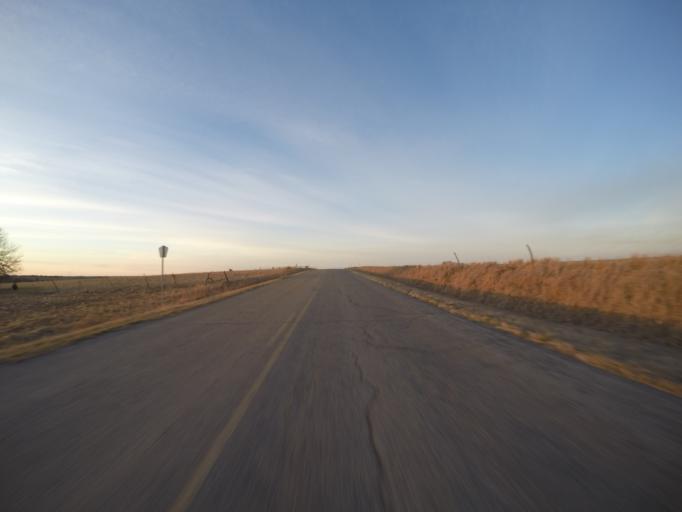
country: US
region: Kansas
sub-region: Clay County
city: Clay Center
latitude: 39.4946
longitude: -96.9966
